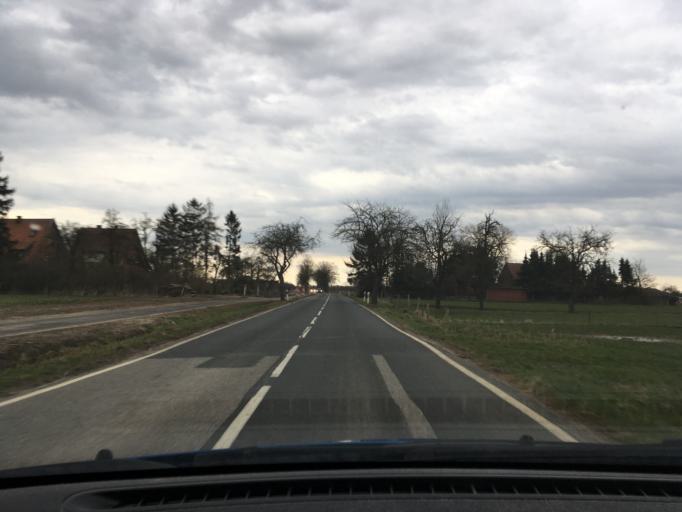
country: DE
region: Lower Saxony
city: Handorf
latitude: 53.3753
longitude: 10.3212
